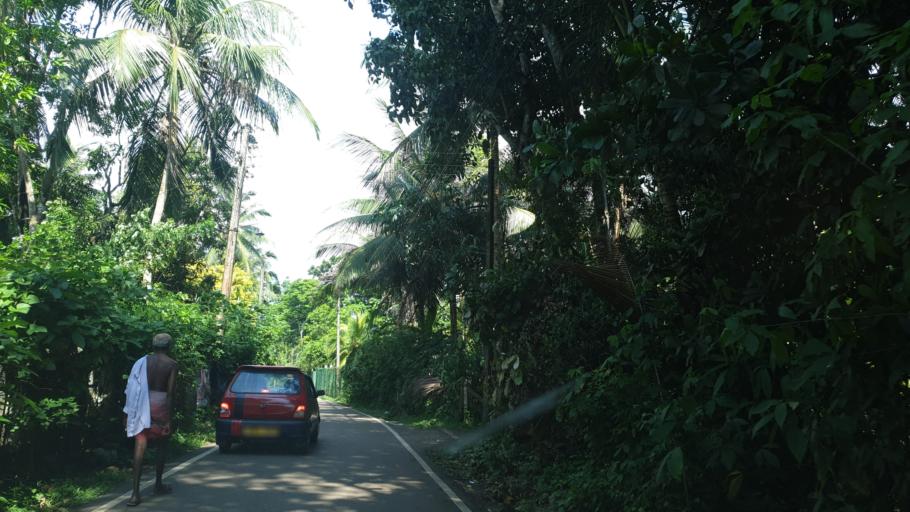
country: LK
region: Western
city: Panadura
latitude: 6.7137
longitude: 79.9620
